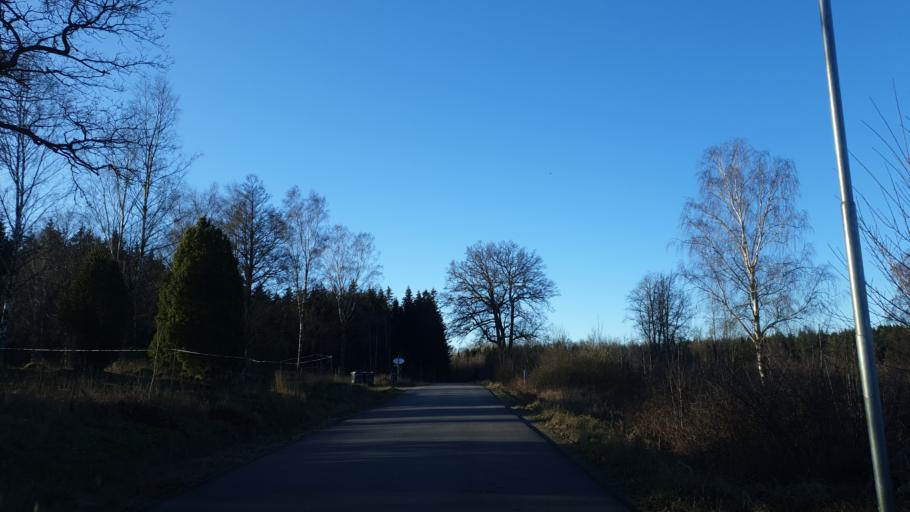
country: SE
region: Blekinge
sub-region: Karlskrona Kommun
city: Nattraby
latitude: 56.2703
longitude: 15.4574
